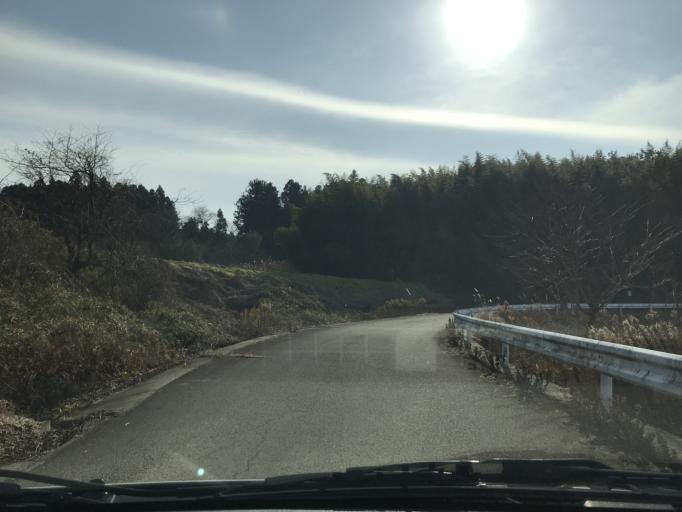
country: JP
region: Miyagi
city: Wakuya
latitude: 38.6974
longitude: 141.1434
